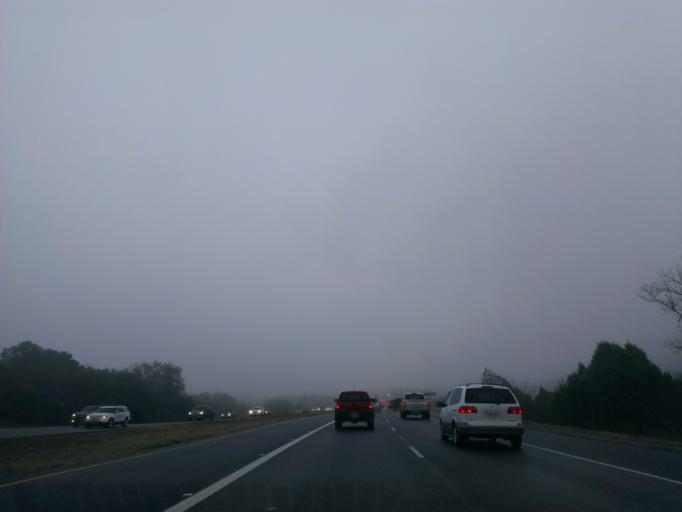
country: US
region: Texas
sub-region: Williamson County
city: Jollyville
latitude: 30.3812
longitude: -97.7741
